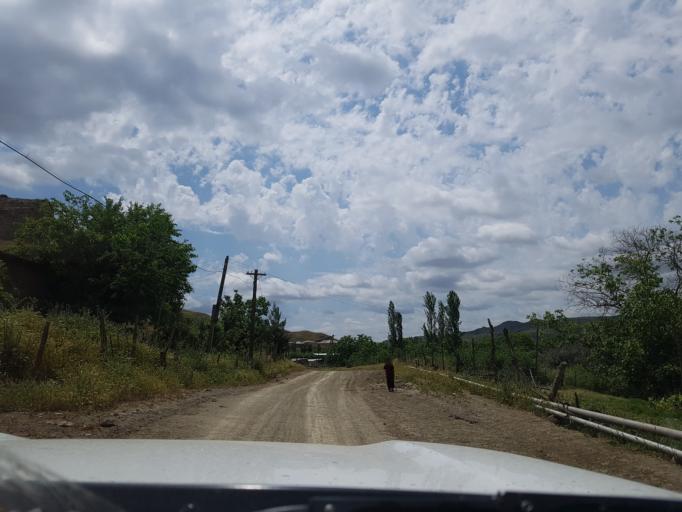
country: TM
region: Ahal
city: Baharly
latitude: 38.2034
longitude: 57.0021
